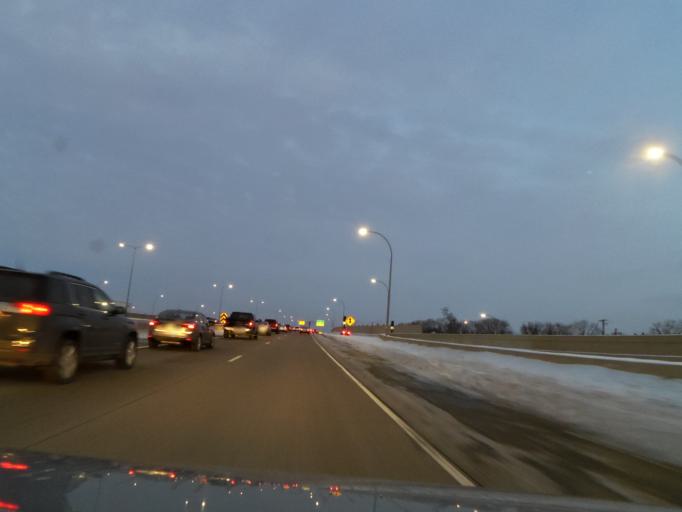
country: US
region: Minnesota
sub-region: Hennepin County
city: Richfield
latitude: 44.8898
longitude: -93.2902
